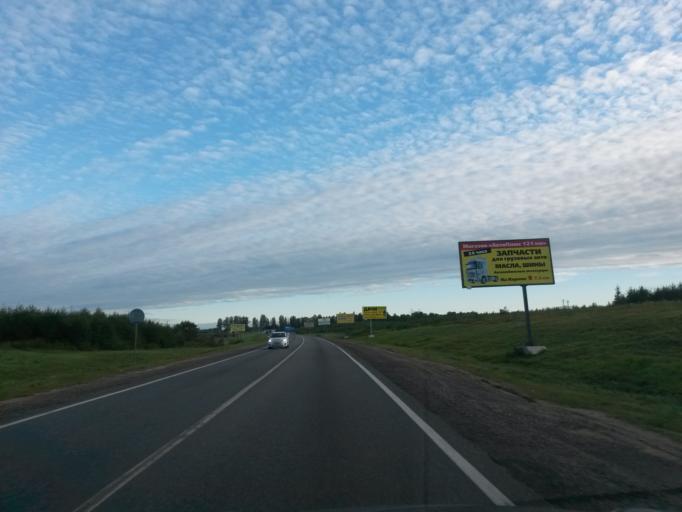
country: RU
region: Vladimir
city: Strunino
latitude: 56.5570
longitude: 38.5868
